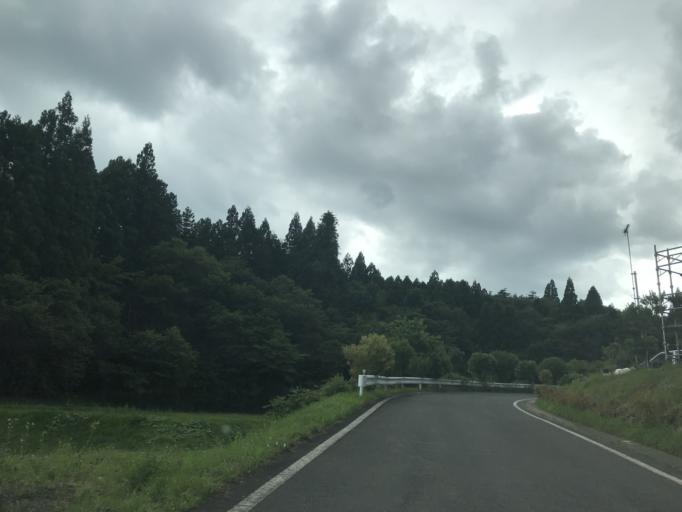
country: JP
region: Iwate
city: Ichinoseki
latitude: 38.9531
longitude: 141.0465
